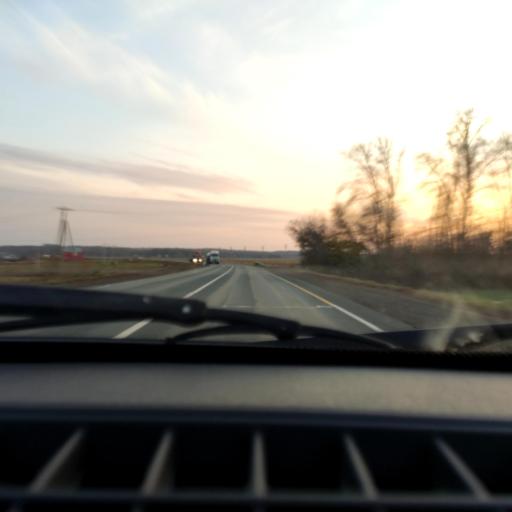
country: RU
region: Bashkortostan
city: Avdon
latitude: 54.6787
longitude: 55.7314
